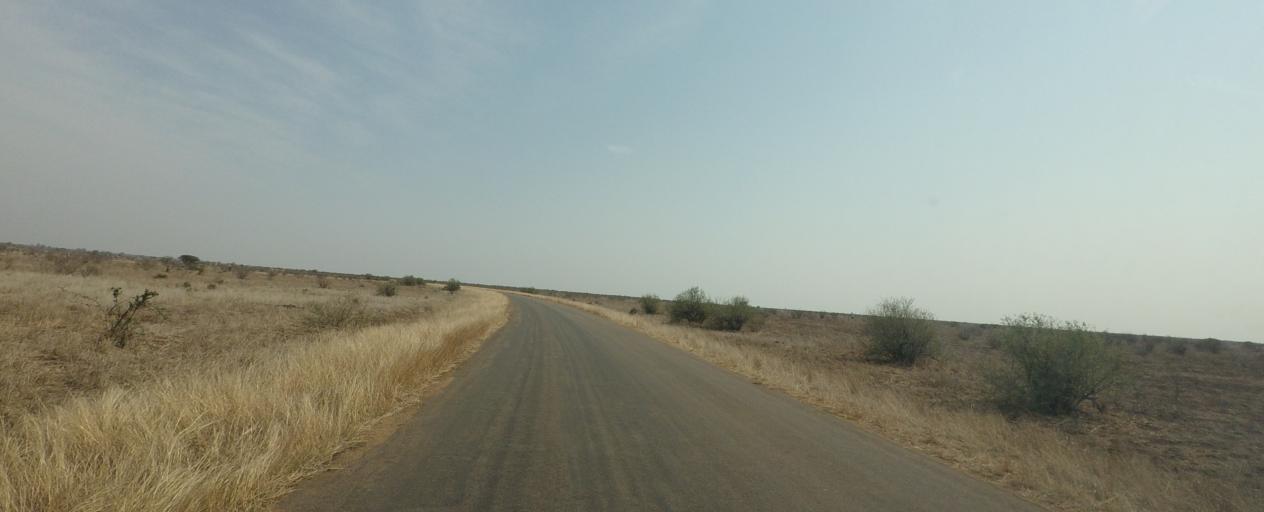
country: ZA
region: Limpopo
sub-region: Mopani District Municipality
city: Phalaborwa
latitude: -24.2619
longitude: 31.7305
